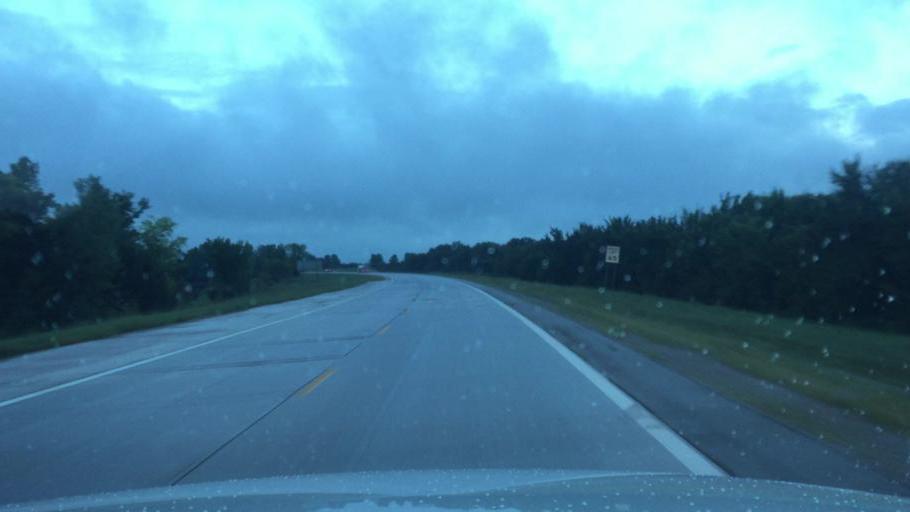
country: US
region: Kansas
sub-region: Neosho County
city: Chanute
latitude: 37.7190
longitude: -95.4780
